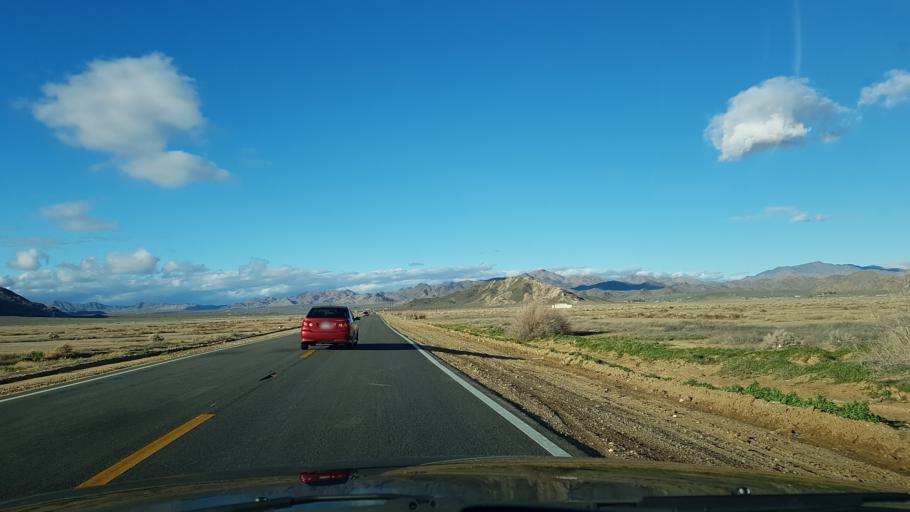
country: US
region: California
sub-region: San Bernardino County
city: Lucerne Valley
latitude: 34.5166
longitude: -116.9453
